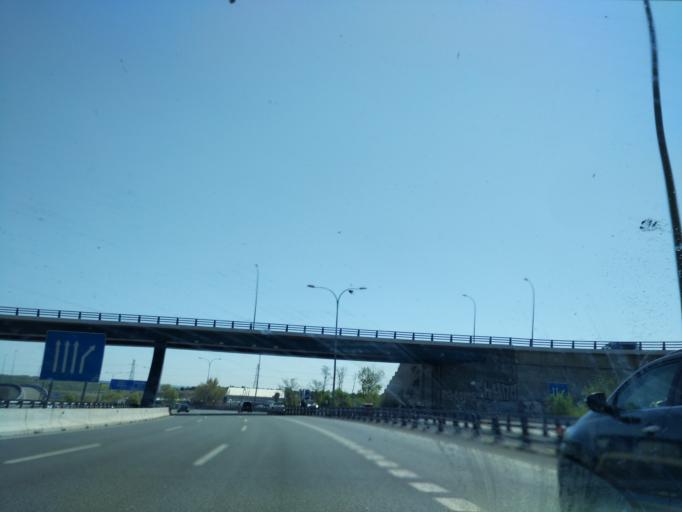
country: ES
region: Madrid
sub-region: Provincia de Madrid
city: Villa de Vallecas
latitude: 40.3680
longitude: -3.5860
